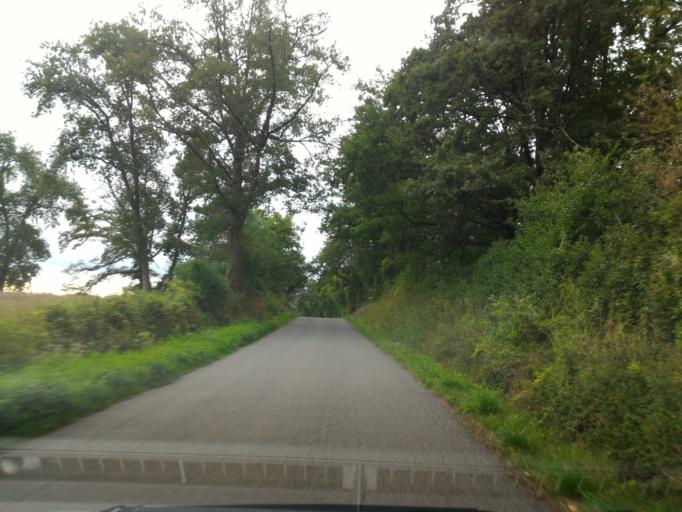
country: FR
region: Poitou-Charentes
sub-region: Departement de la Charente
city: Etagnac
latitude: 45.9348
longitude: 0.8112
